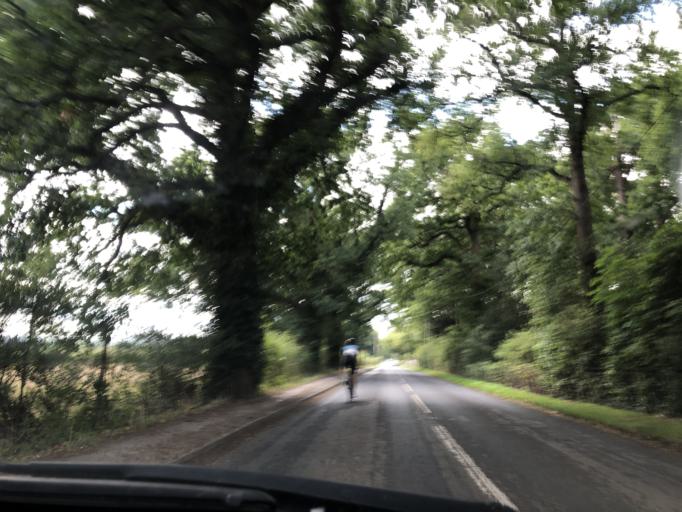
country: GB
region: England
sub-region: Kent
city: Edenbridge
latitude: 51.2260
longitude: 0.0603
